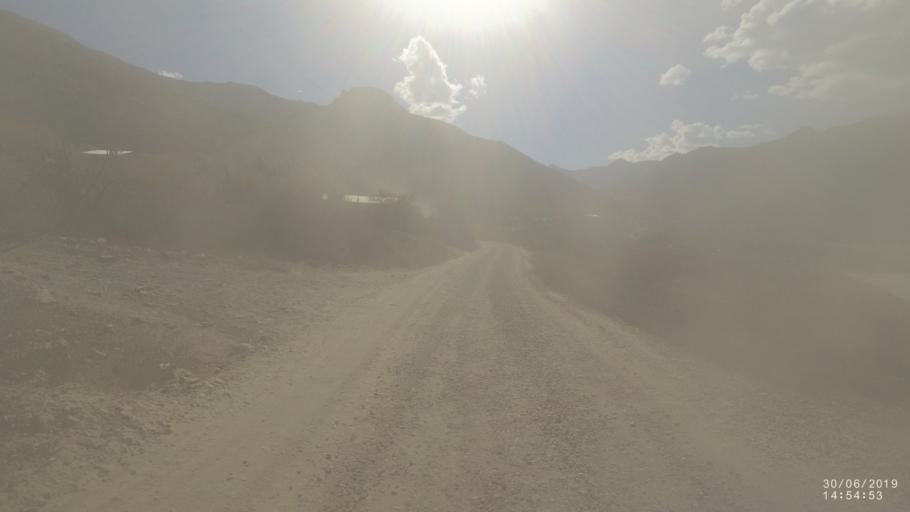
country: BO
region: Cochabamba
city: Irpa Irpa
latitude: -17.7562
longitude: -66.3510
